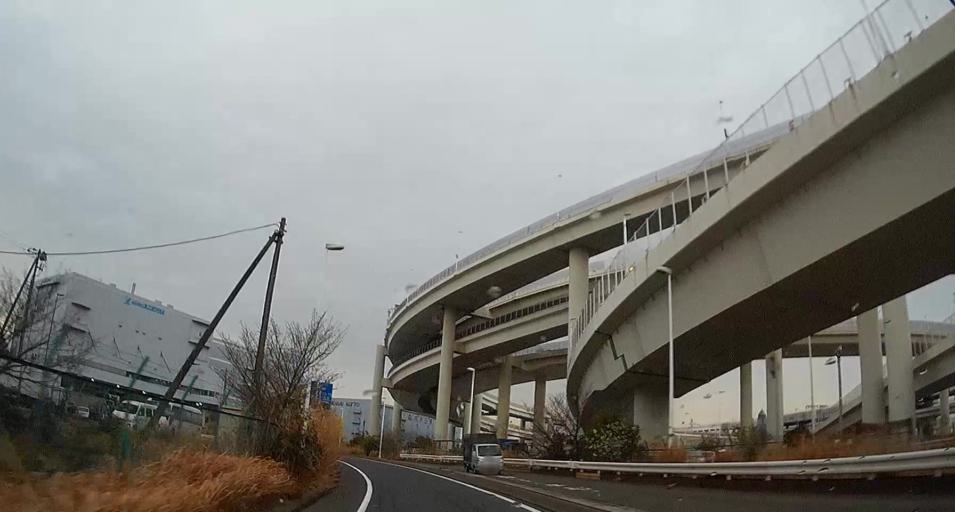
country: JP
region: Kanagawa
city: Yokohama
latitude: 35.4629
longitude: 139.6839
